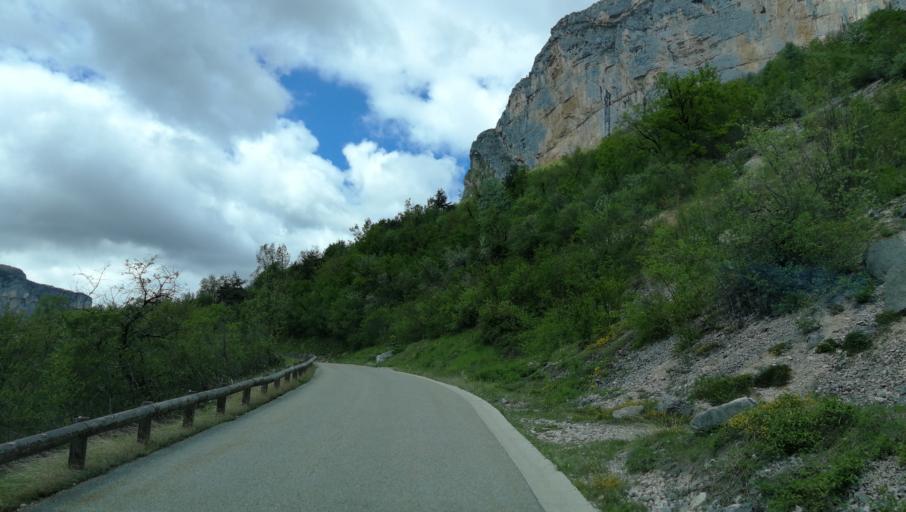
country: FR
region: Rhone-Alpes
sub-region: Departement de l'Isere
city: Pont-en-Royans
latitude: 45.0642
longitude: 5.4221
